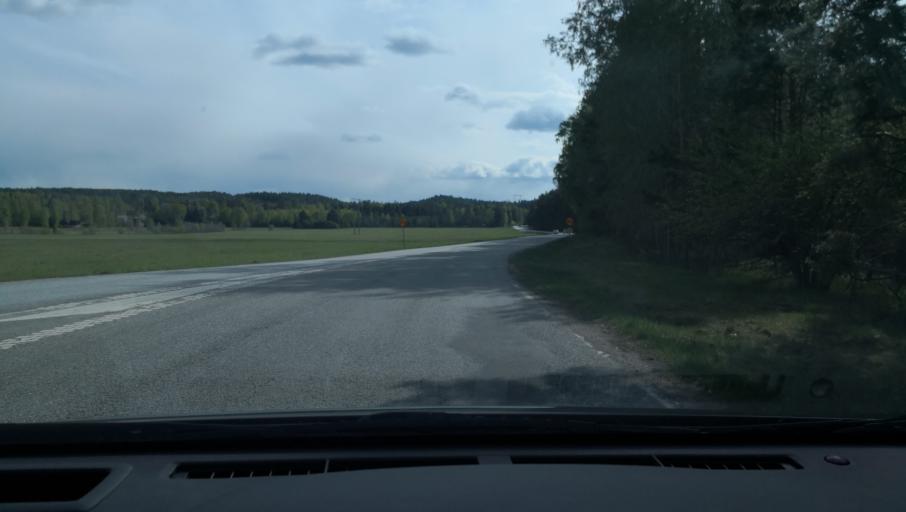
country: SE
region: OErebro
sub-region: Askersunds Kommun
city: Asbro
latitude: 59.0528
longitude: 15.0498
